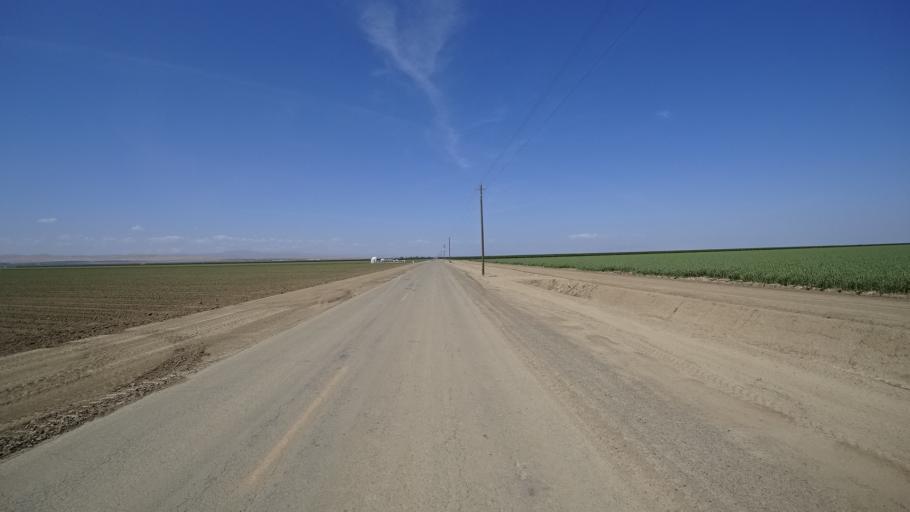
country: US
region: California
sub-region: Kings County
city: Kettleman City
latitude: 36.0942
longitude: -119.9738
